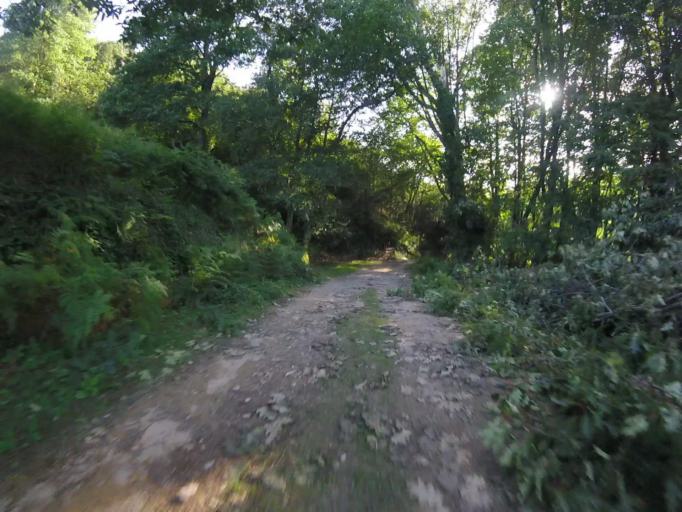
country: ES
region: Basque Country
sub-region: Provincia de Guipuzcoa
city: Irun
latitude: 43.3141
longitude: -1.7520
